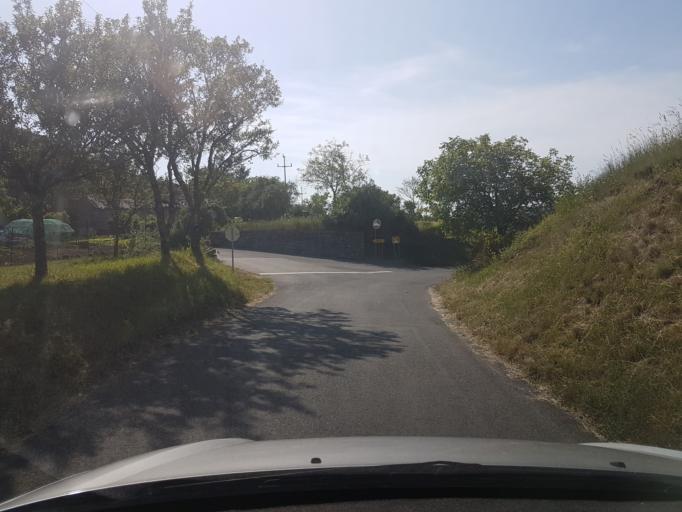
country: SI
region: Vipava
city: Vipava
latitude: 45.7698
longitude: 13.9630
